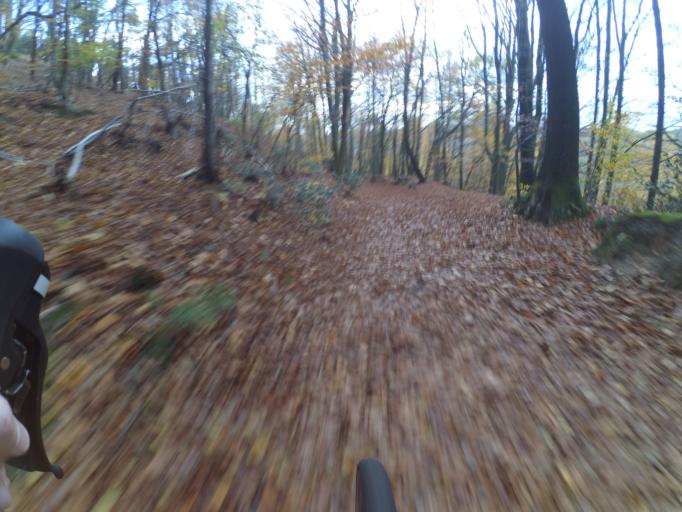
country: DE
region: North Rhine-Westphalia
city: Ibbenburen
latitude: 52.2322
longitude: 7.7527
